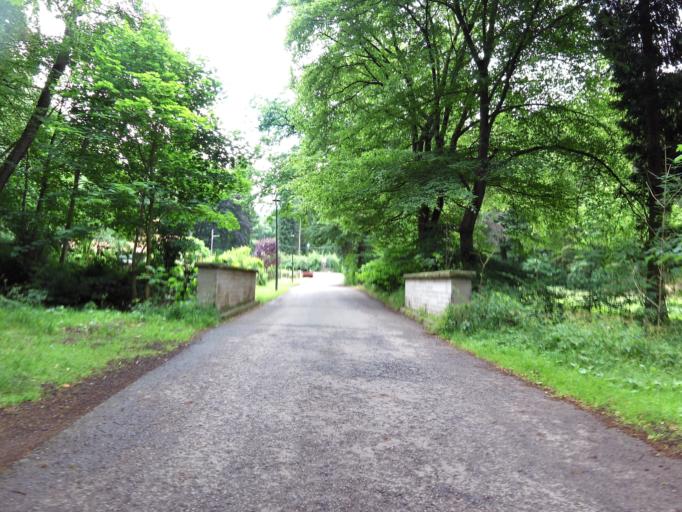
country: DE
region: Thuringia
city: Tabarz
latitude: 50.8670
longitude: 10.5102
